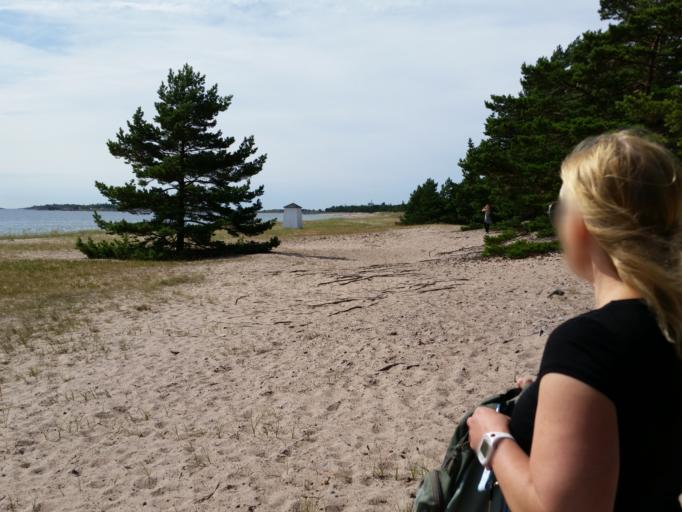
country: FI
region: Uusimaa
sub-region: Raaseporin
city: Hanko
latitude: 59.8232
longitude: 22.9256
